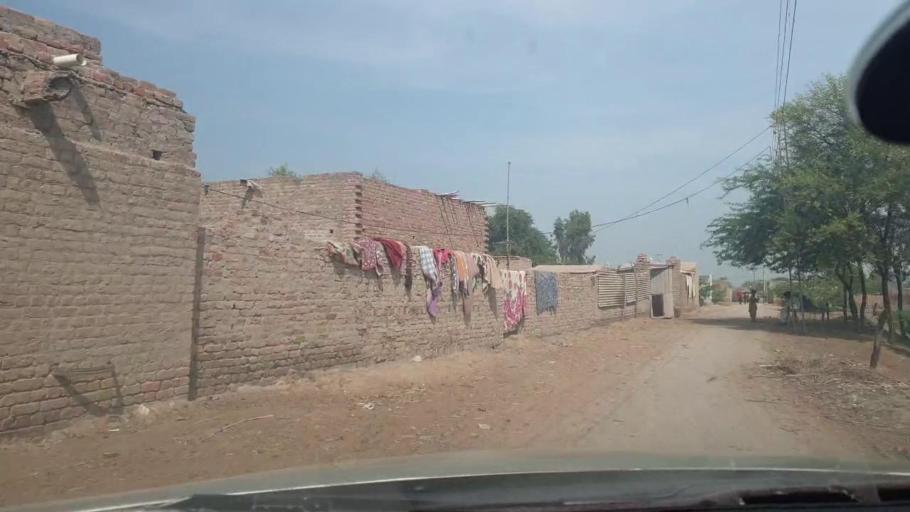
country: PK
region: Sindh
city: Jacobabad
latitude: 28.2952
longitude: 68.4786
